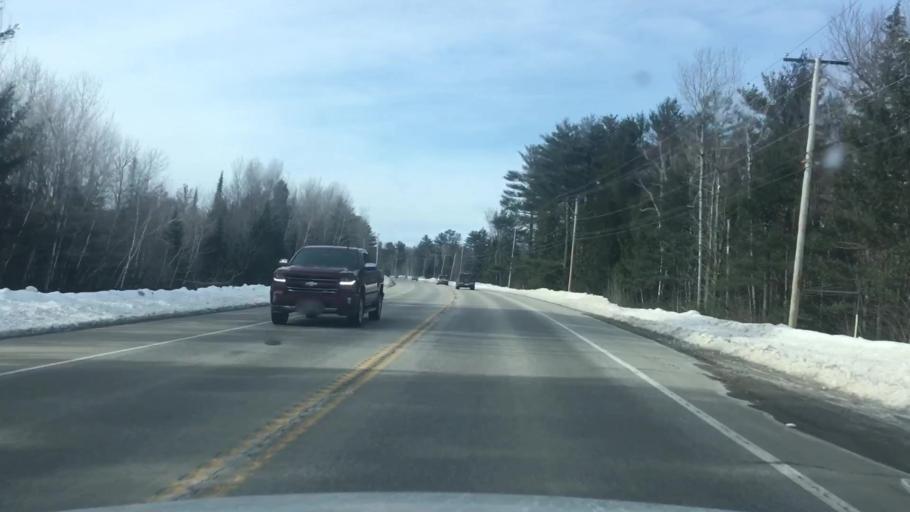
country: US
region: Maine
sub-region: Penobscot County
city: Kenduskeag
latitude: 44.9590
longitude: -68.9547
